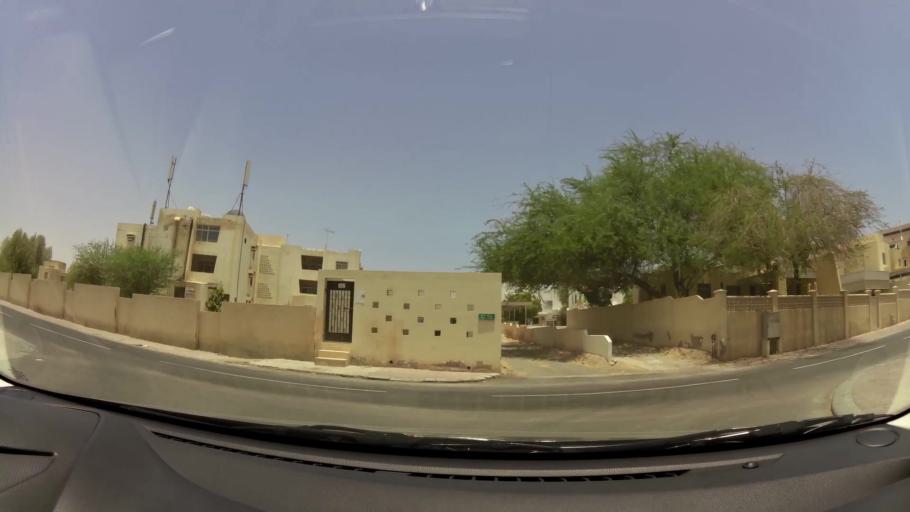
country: OM
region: Muhafazat Masqat
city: Bawshar
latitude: 23.6009
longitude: 58.4598
